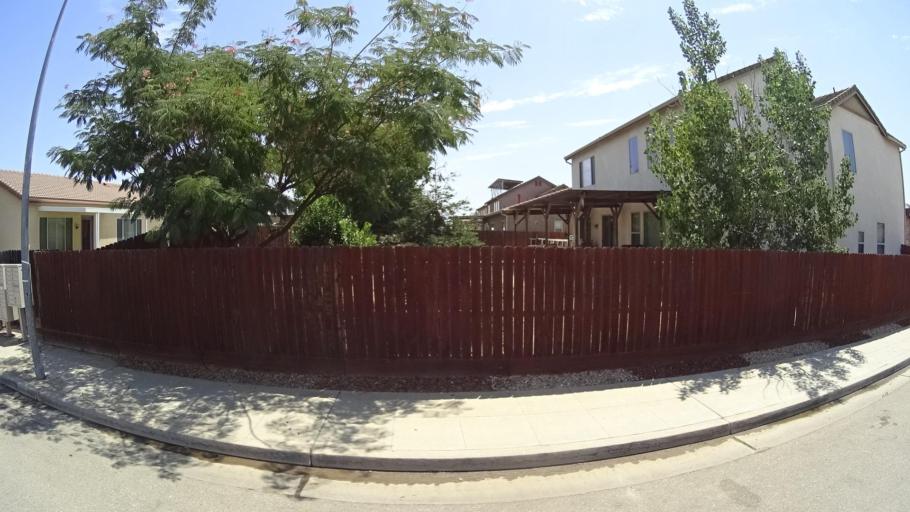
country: US
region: California
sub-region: Fresno County
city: Tarpey Village
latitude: 36.7836
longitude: -119.6591
